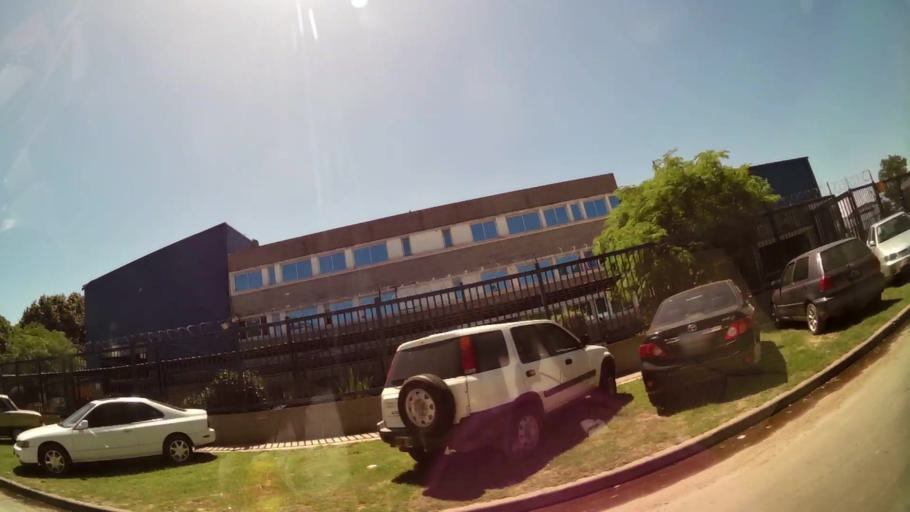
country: AR
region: Buenos Aires
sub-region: Partido de Tigre
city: Tigre
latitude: -34.4825
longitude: -58.6495
